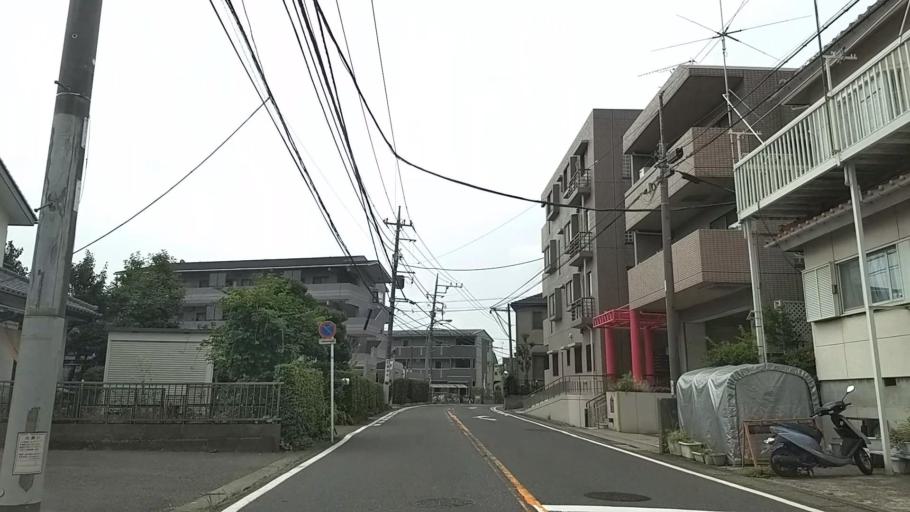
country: JP
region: Kanagawa
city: Yokohama
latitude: 35.5157
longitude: 139.5584
